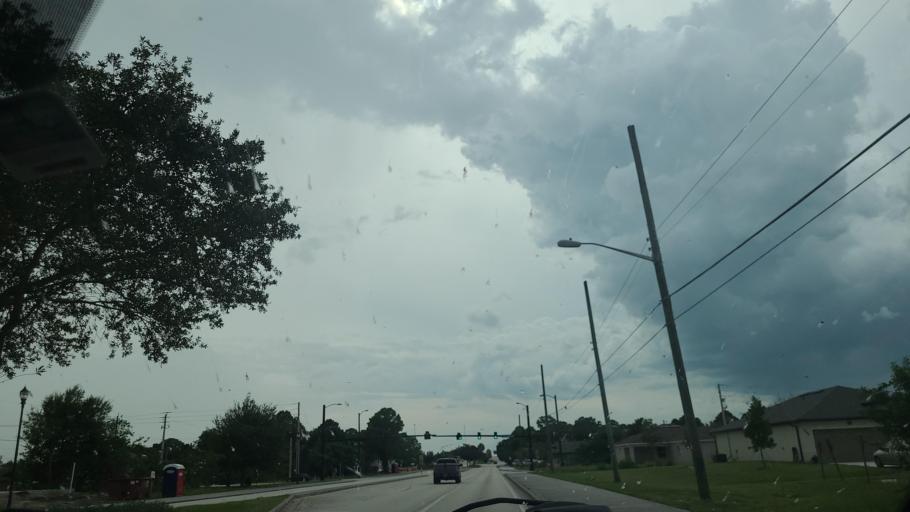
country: US
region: Florida
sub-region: Saint Lucie County
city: Port Saint Lucie
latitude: 27.2098
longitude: -80.3907
